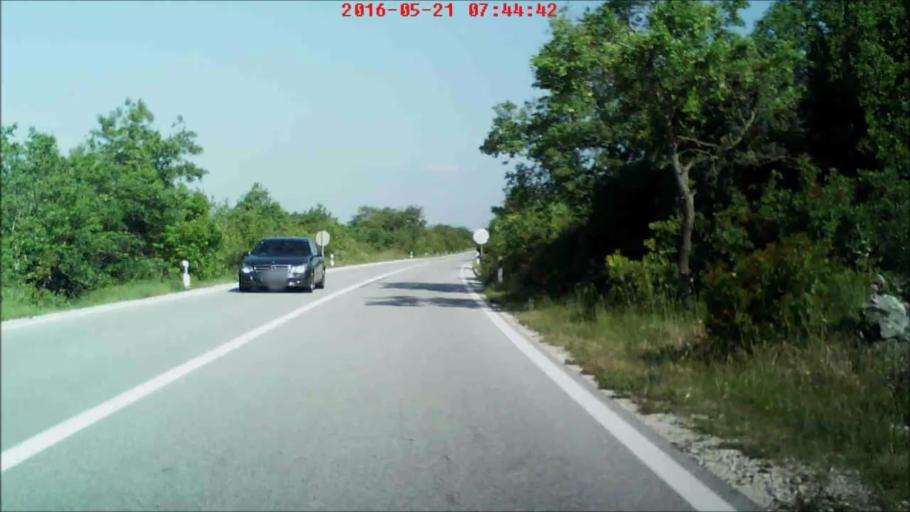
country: HR
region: Dubrovacko-Neretvanska
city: Podgora
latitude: 42.8176
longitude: 17.7751
